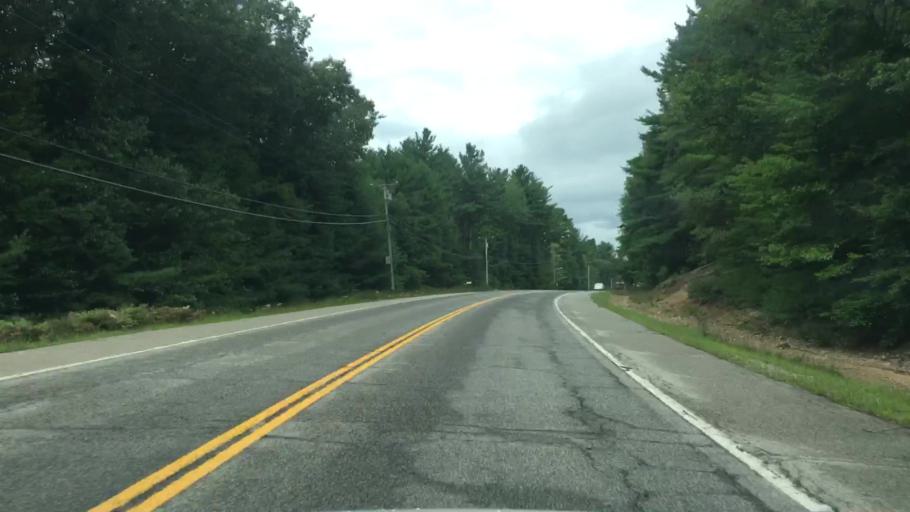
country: US
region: Maine
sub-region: York County
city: South Sanford
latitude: 43.3784
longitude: -70.7405
